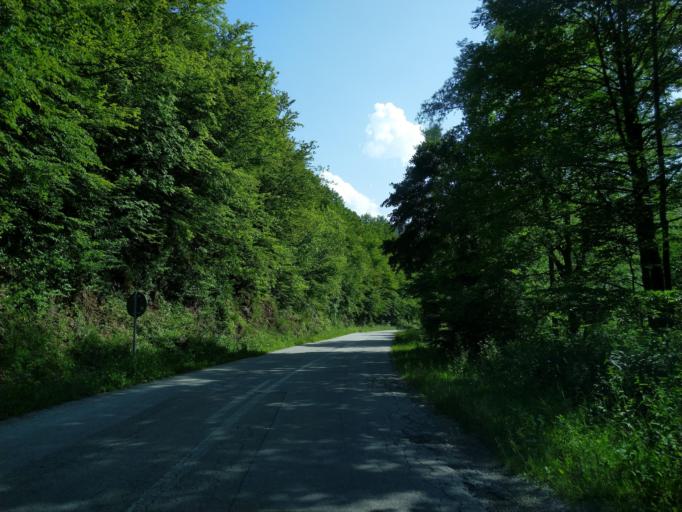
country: RS
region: Central Serbia
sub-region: Zlatiborski Okrug
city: Bajina Basta
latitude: 43.8615
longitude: 19.6255
